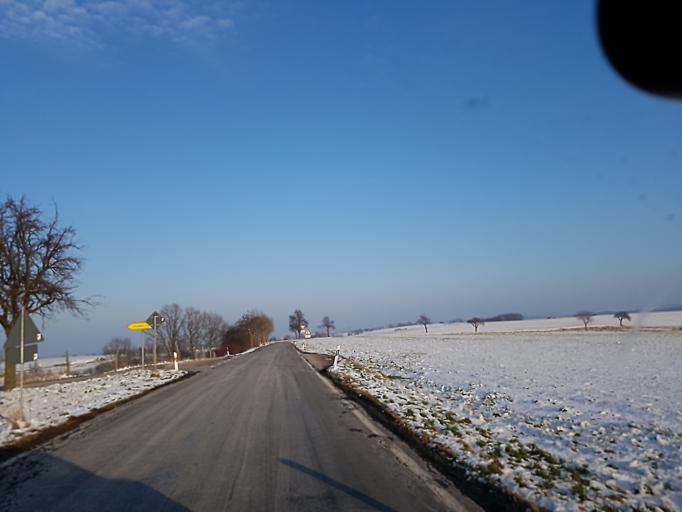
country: DE
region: Saxony
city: Grossweitzschen
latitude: 51.2030
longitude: 13.0804
